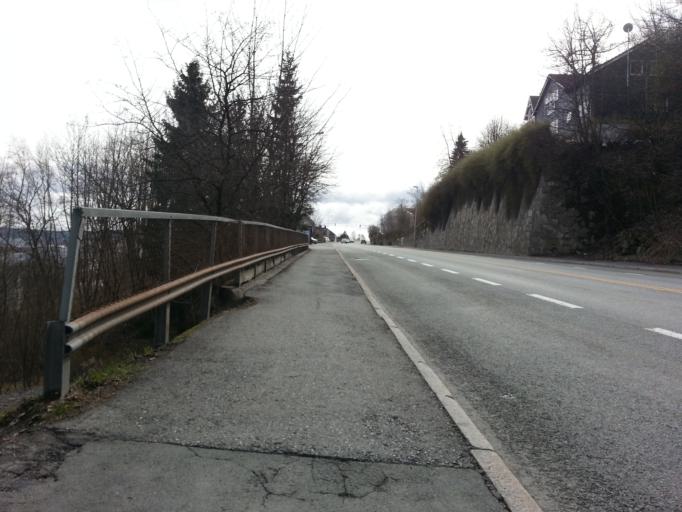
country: NO
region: Sor-Trondelag
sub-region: Trondheim
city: Trondheim
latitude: 63.4253
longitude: 10.3700
